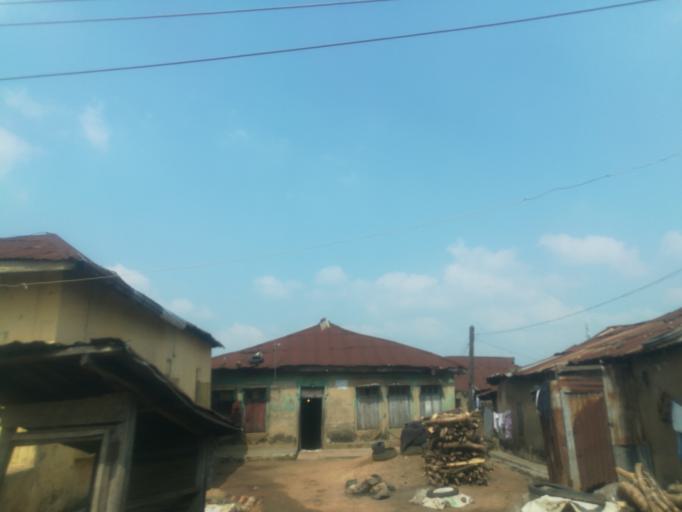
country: NG
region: Oyo
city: Ibadan
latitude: 7.3924
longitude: 3.9073
